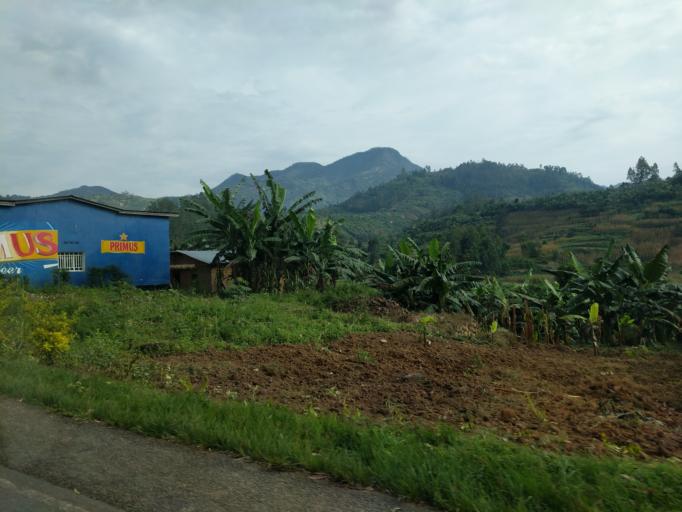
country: RW
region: Northern Province
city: Musanze
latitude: -1.6505
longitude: 29.8061
